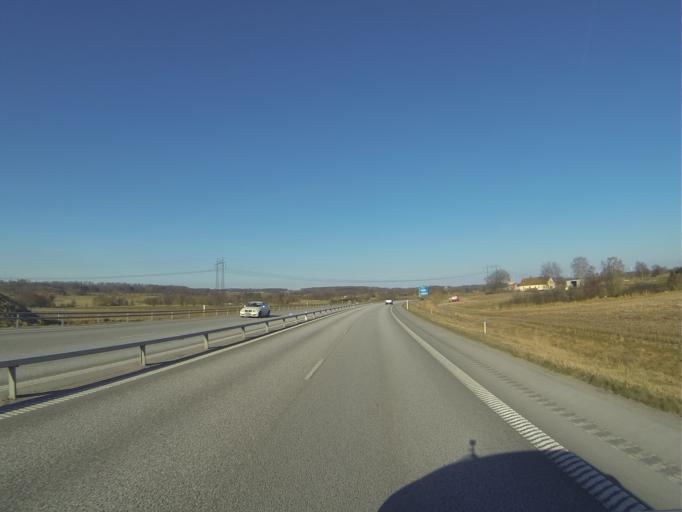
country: SE
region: Skane
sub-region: Hoors Kommun
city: Loberod
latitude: 55.8010
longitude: 13.4522
